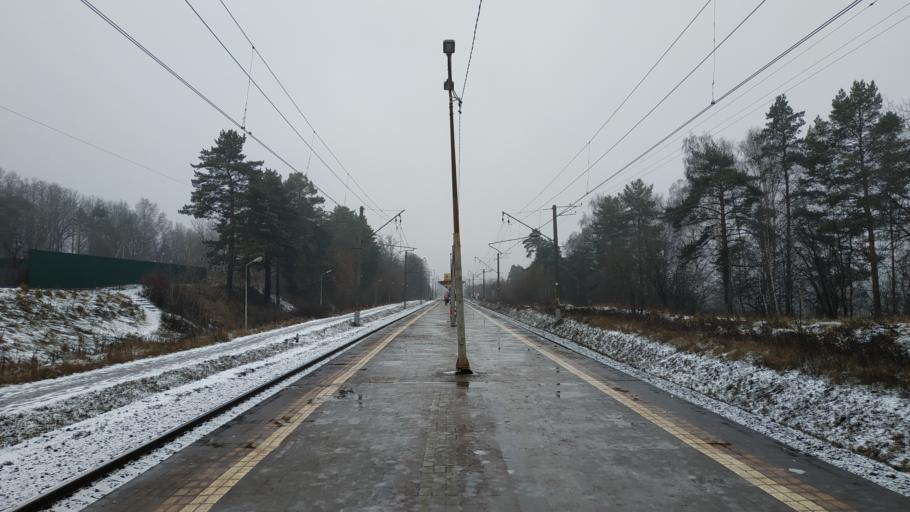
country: RU
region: Moskovskaya
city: Dedenevo
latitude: 56.2447
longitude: 37.5117
